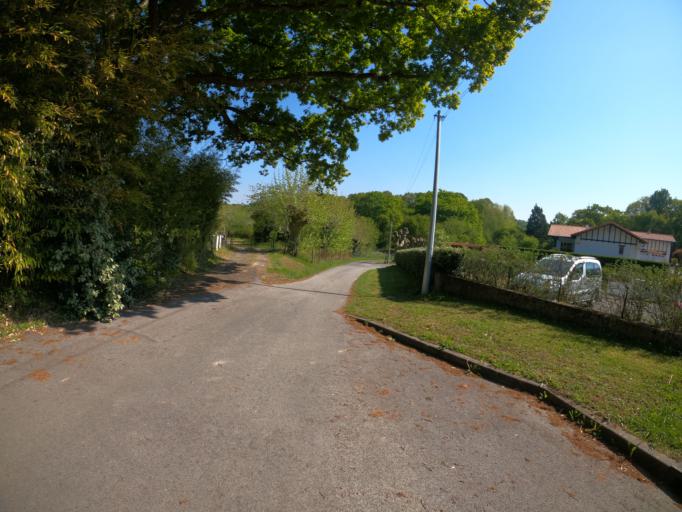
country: FR
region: Aquitaine
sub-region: Departement des Pyrenees-Atlantiques
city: Bassussarry
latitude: 43.4367
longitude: -1.4991
